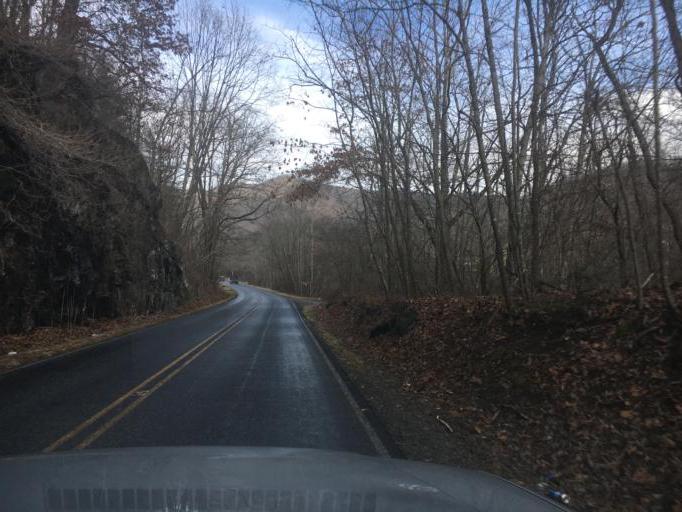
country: US
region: North Carolina
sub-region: Haywood County
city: Canton
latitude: 35.4360
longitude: -82.8147
